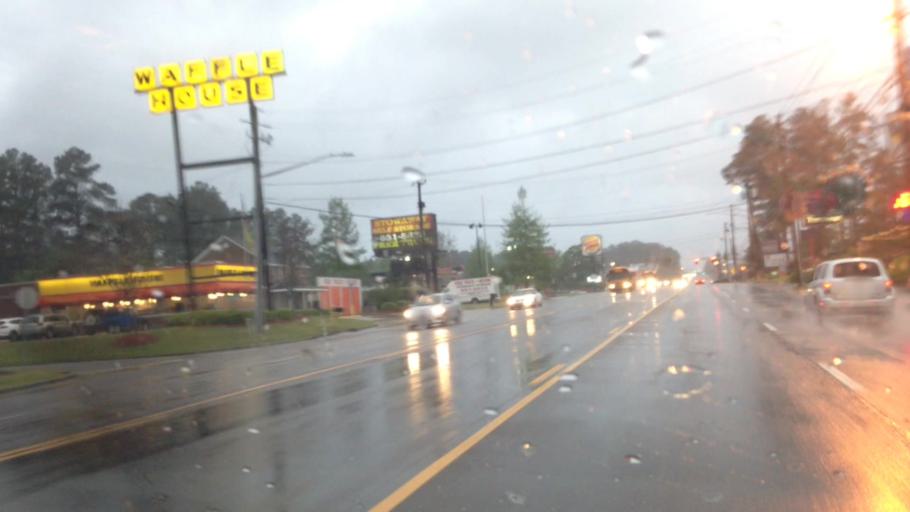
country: US
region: Georgia
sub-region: Columbia County
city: Martinez
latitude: 33.5128
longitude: -82.0484
